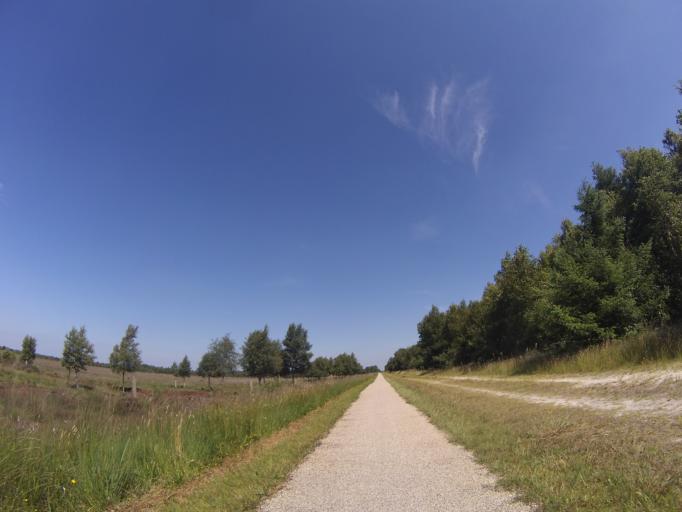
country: DE
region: Lower Saxony
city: Twist
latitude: 52.6814
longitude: 7.0590
